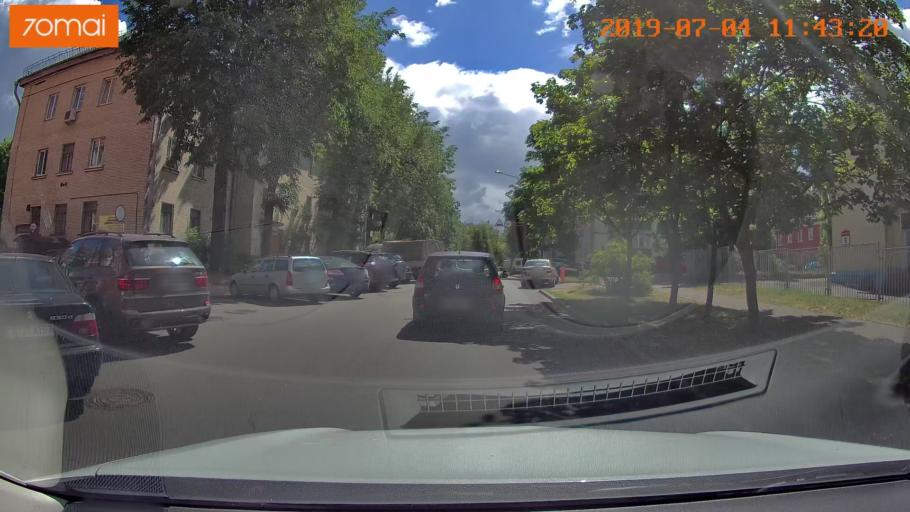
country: BY
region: Minsk
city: Minsk
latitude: 53.9274
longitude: 27.5997
